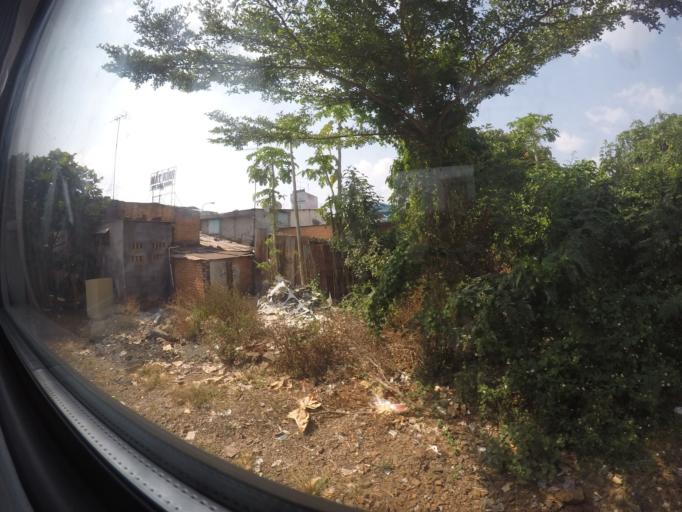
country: VN
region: Dong Nai
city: Long Khanh
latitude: 10.9335
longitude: 107.2437
